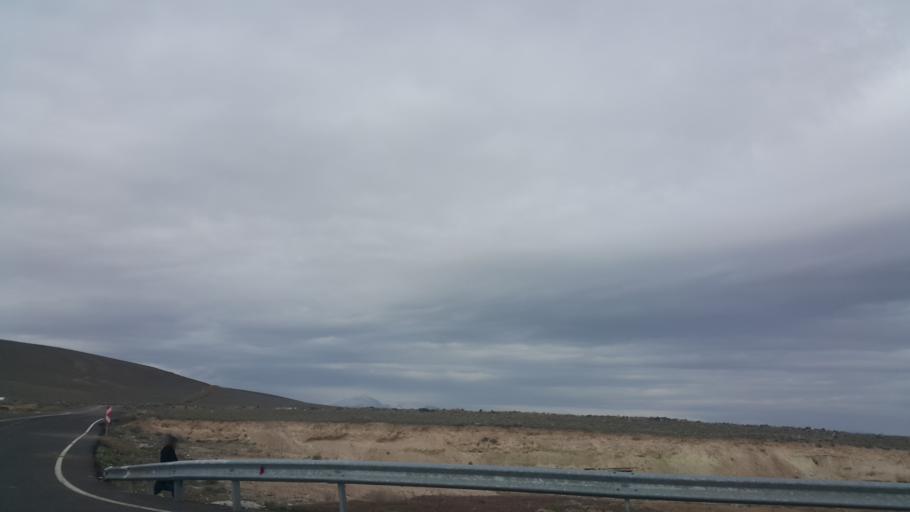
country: TR
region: Aksaray
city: Taspinar
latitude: 37.9358
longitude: 34.1006
